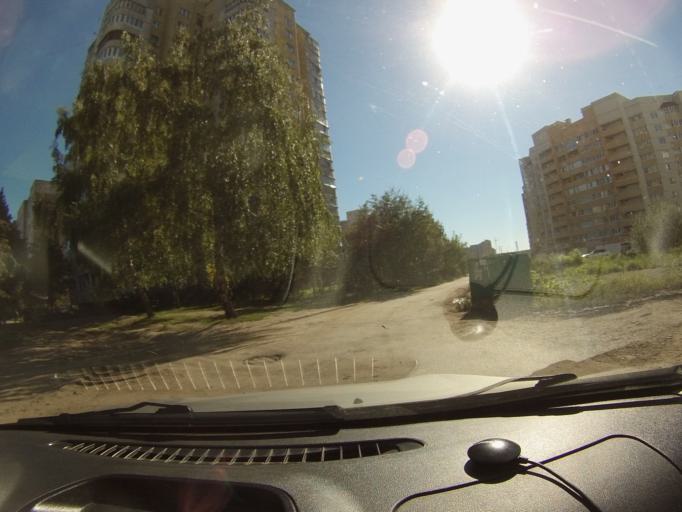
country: RU
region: Tambov
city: Tambov
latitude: 52.7650
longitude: 41.4031
